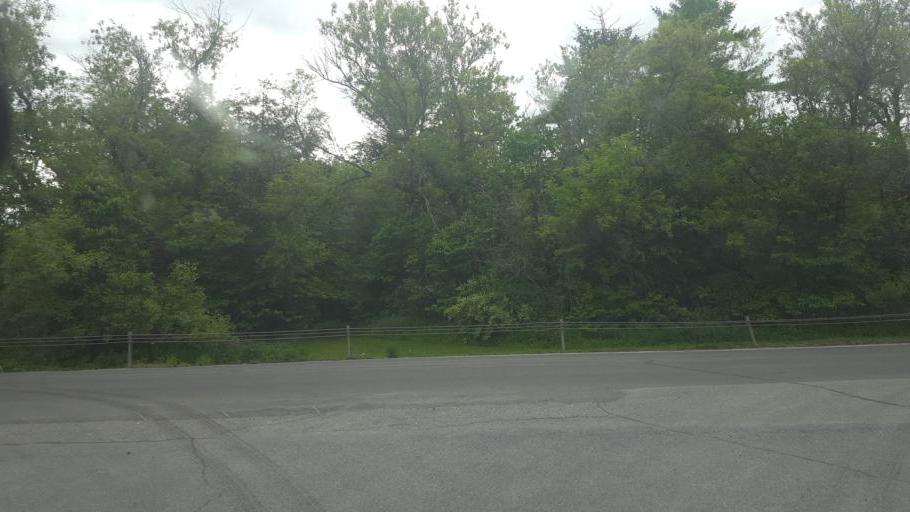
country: US
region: New York
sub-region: Otsego County
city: Richfield Springs
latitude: 42.8622
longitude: -74.9757
